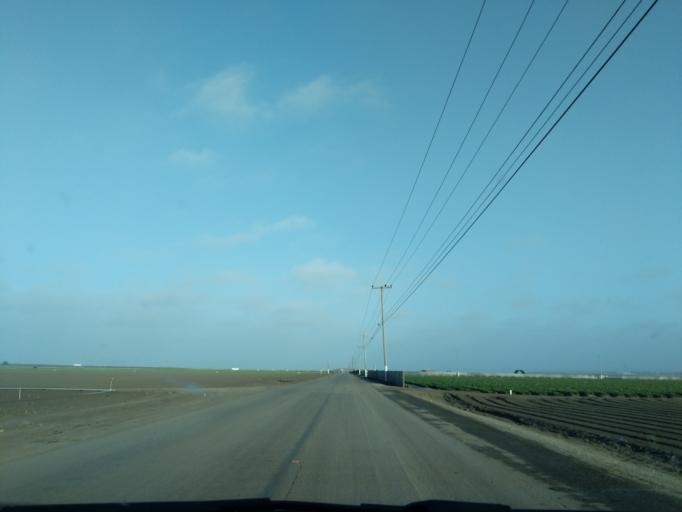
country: US
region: California
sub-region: Monterey County
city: Castroville
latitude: 36.7555
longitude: -121.7819
